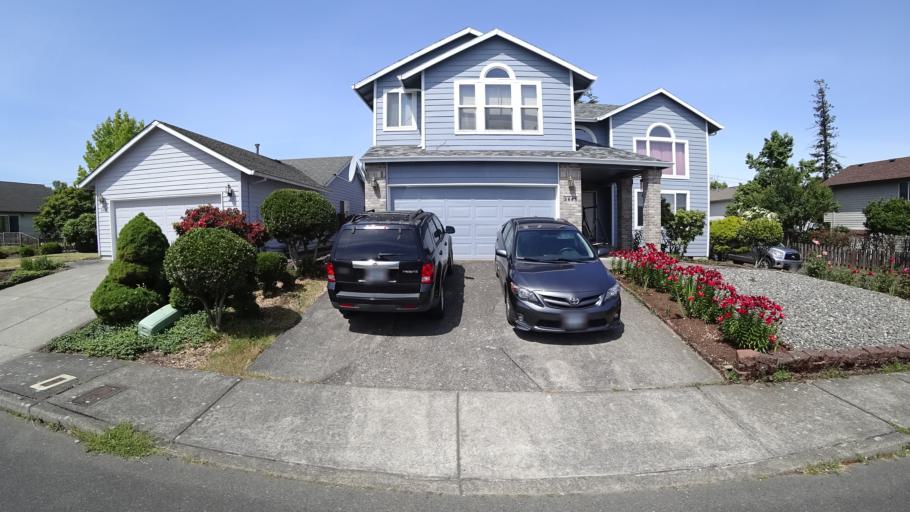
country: US
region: Oregon
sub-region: Multnomah County
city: Fairview
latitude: 45.5483
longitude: -122.5090
